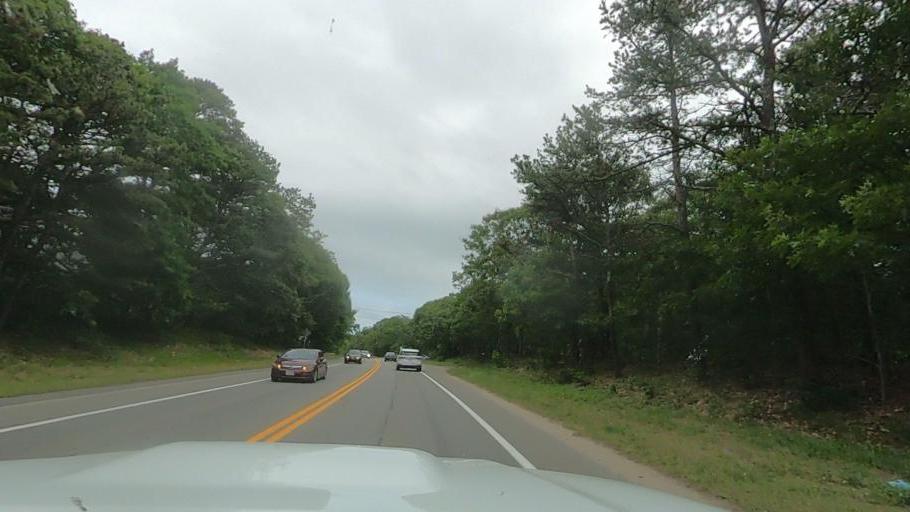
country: US
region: Massachusetts
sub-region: Barnstable County
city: Wellfleet
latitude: 41.9193
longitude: -70.0054
